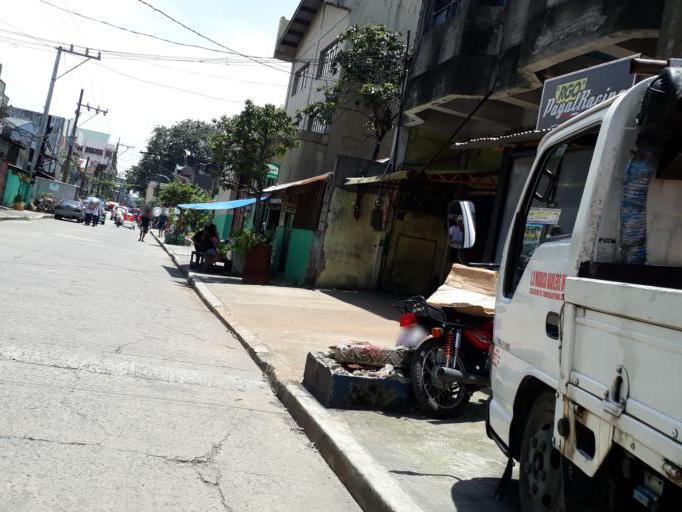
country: PH
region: Calabarzon
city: Del Monte
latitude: 14.6500
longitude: 120.9860
